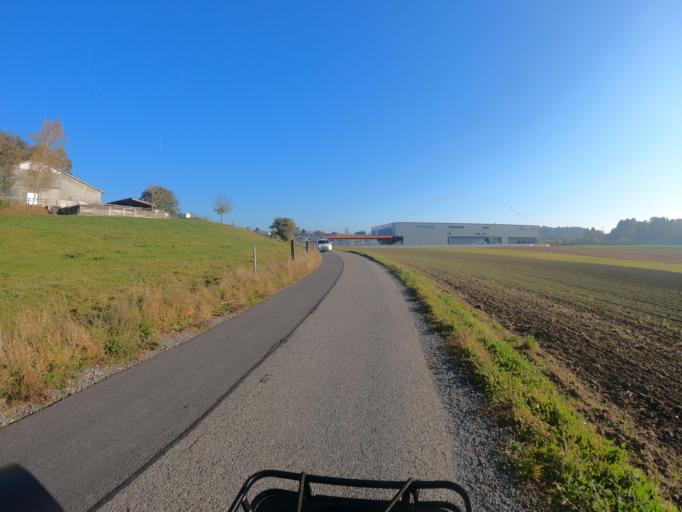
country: CH
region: Zurich
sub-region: Bezirk Affoltern
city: Affoltern / Oberdorf
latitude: 47.2781
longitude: 8.4368
